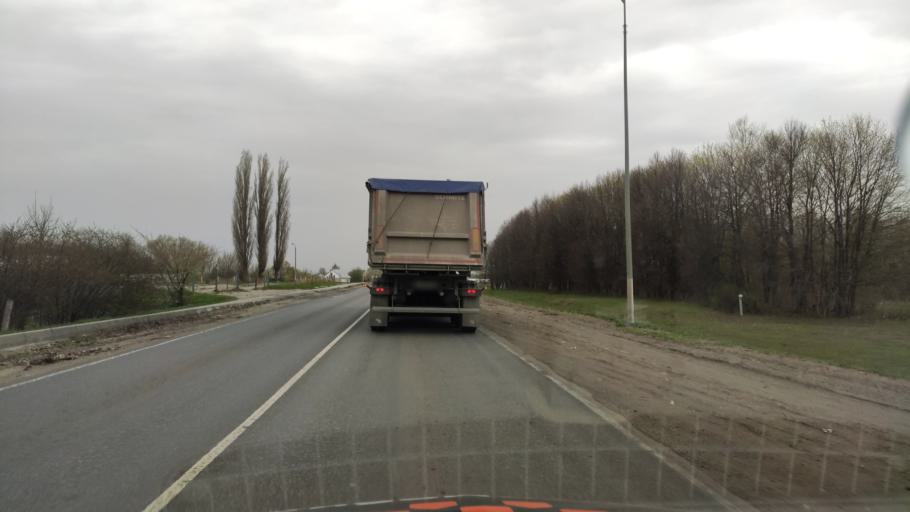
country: RU
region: Kursk
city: Gorshechnoye
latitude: 51.5252
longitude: 38.0231
